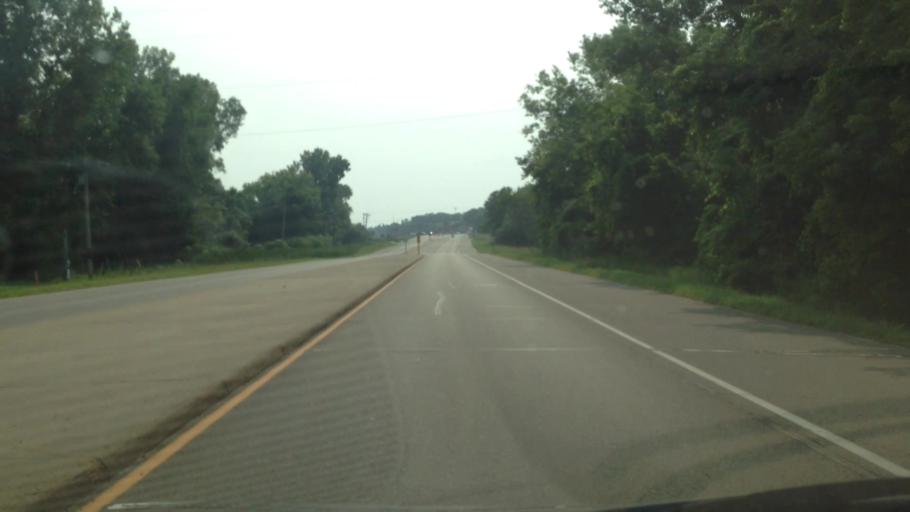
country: US
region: Minnesota
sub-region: Anoka County
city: Lexington
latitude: 45.1439
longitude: -93.1583
